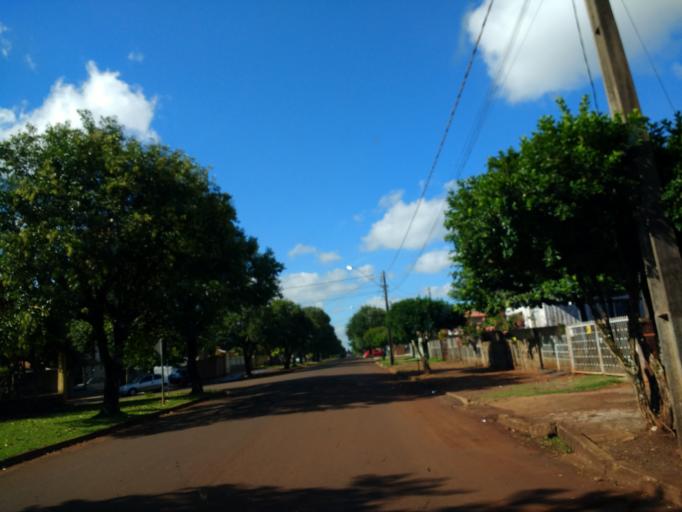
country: BR
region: Parana
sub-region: Palotina
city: Palotina
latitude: -24.4099
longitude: -53.5250
